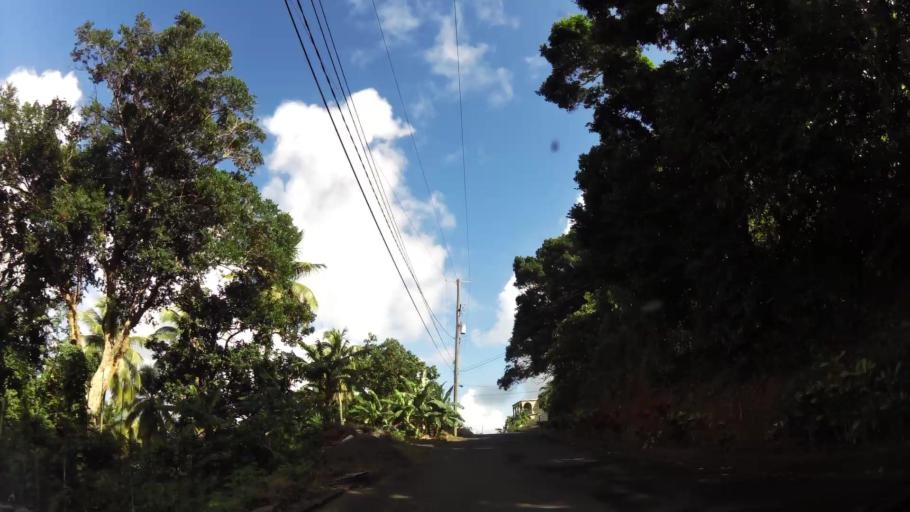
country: DM
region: Saint Andrew
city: Calibishie
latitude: 15.6070
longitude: -61.4018
